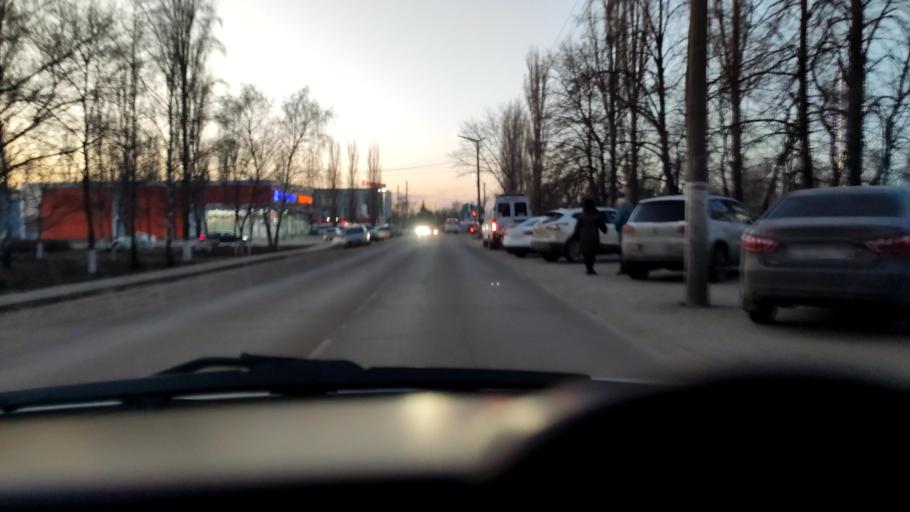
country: RU
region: Voronezj
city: Semiluki
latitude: 51.7005
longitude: 39.0190
